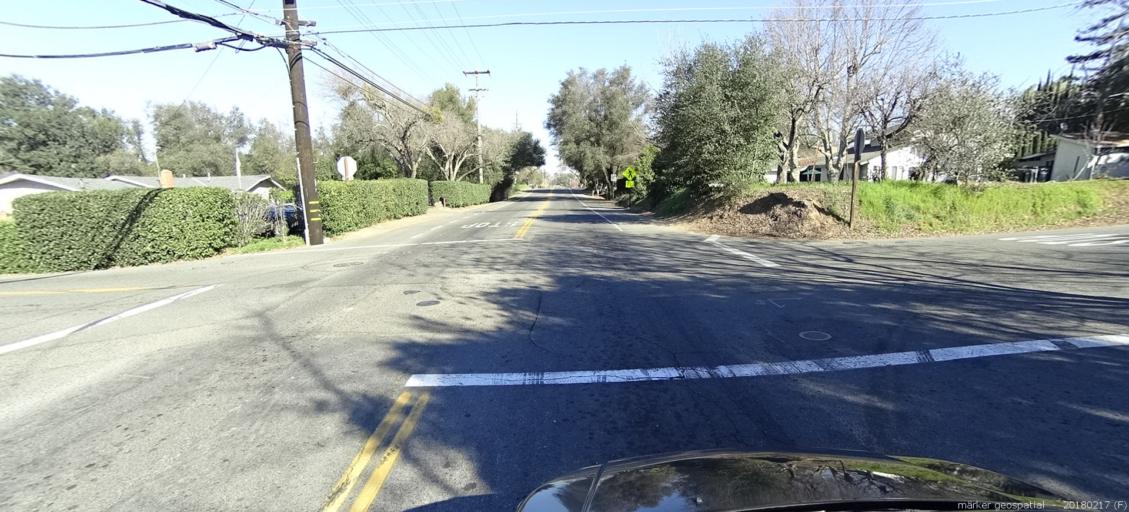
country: US
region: California
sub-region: Sacramento County
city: Orangevale
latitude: 38.6925
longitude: -121.2018
